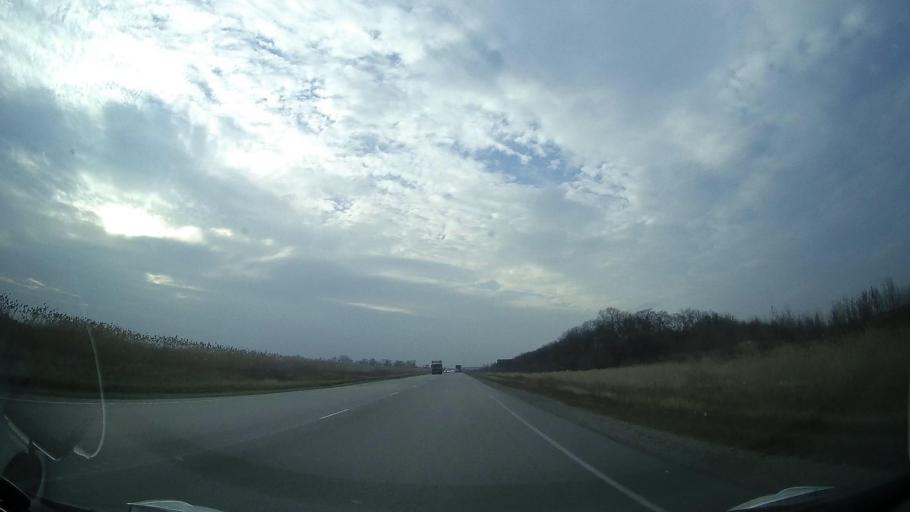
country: RU
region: Rostov
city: Ol'ginskaya
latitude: 47.1310
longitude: 39.9401
